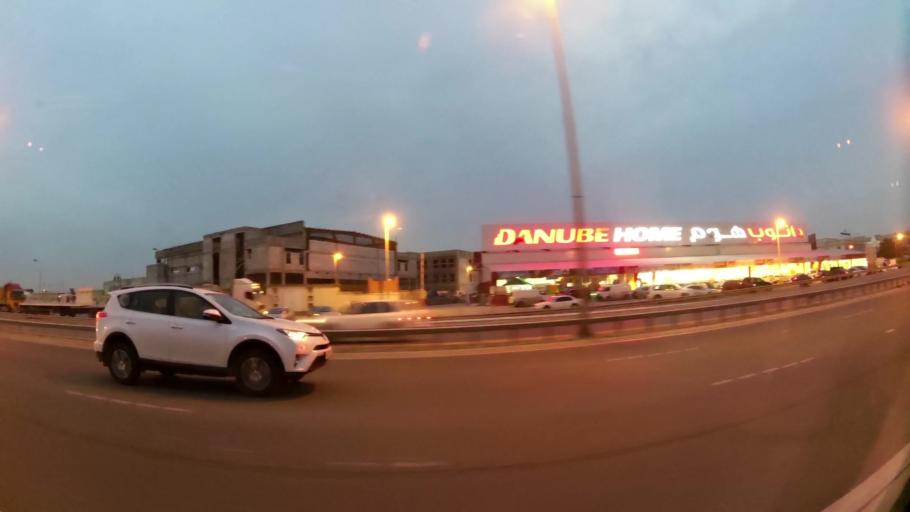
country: BH
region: Northern
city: Madinat `Isa
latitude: 26.1785
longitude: 50.5394
